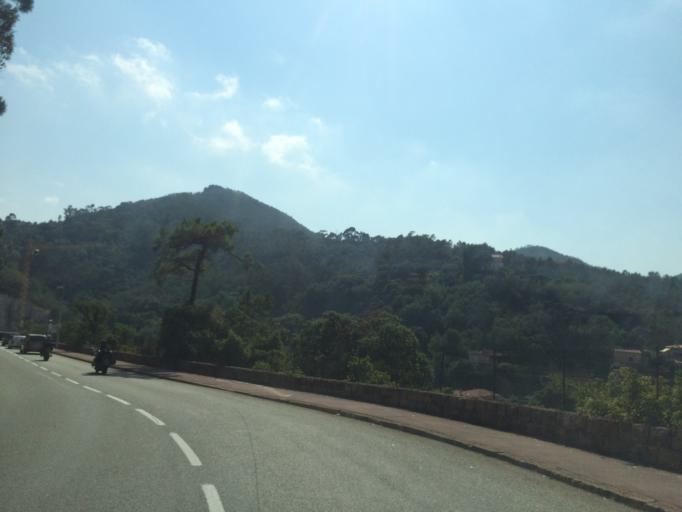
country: FR
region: Provence-Alpes-Cote d'Azur
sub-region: Departement des Alpes-Maritimes
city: Theoule-sur-Mer
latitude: 43.5060
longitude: 6.9411
